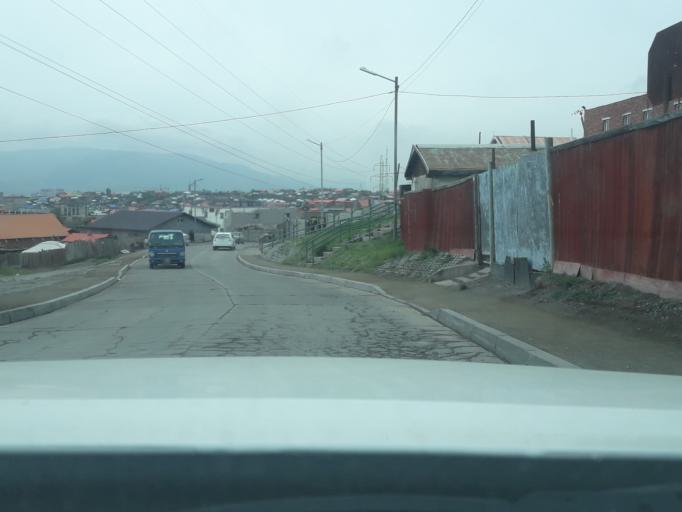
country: MN
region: Ulaanbaatar
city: Ulaanbaatar
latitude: 47.9485
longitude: 106.9043
